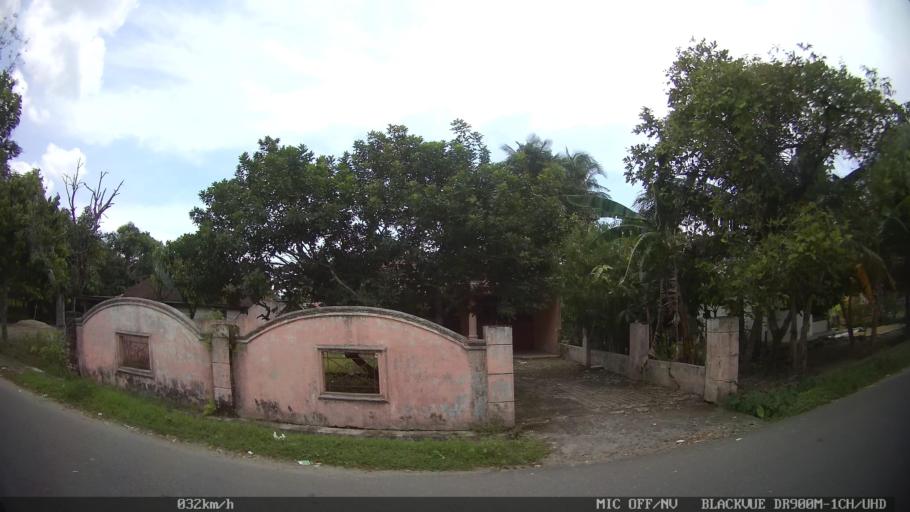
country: ID
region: North Sumatra
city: Binjai
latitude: 3.6279
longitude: 98.5125
